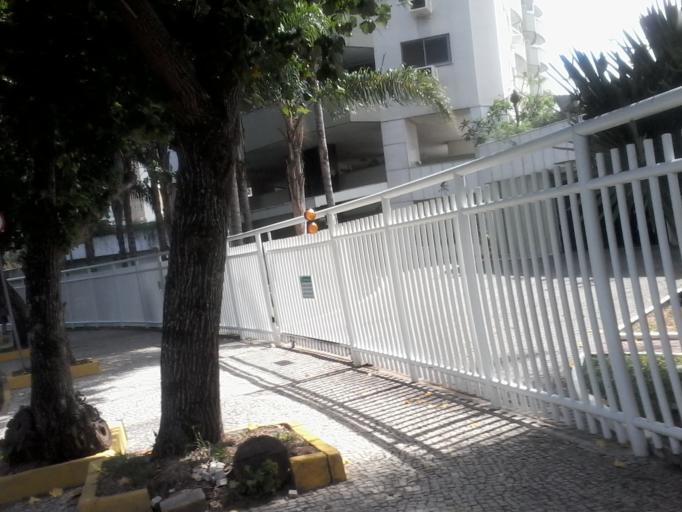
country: BR
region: Rio de Janeiro
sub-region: Nilopolis
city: Nilopolis
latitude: -23.0206
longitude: -43.4865
